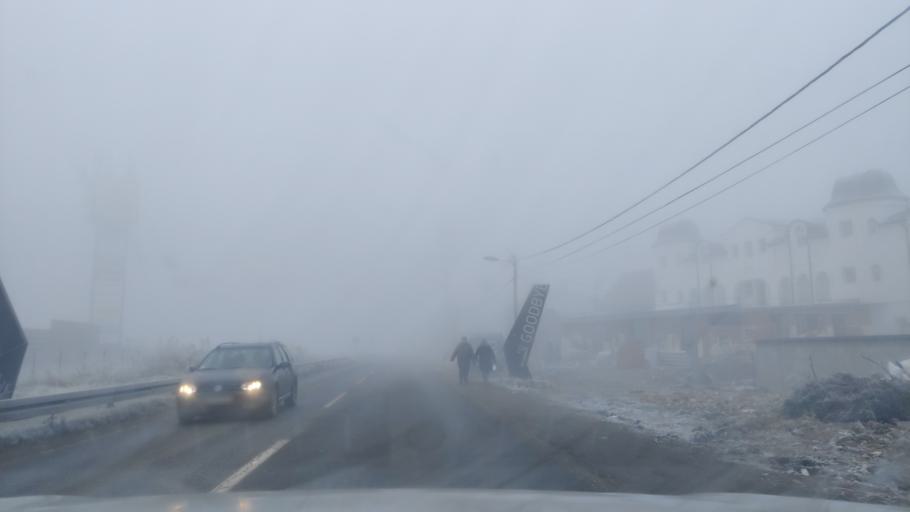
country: RS
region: Central Serbia
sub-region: Belgrade
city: Stari Grad
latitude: 44.8892
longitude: 20.4597
